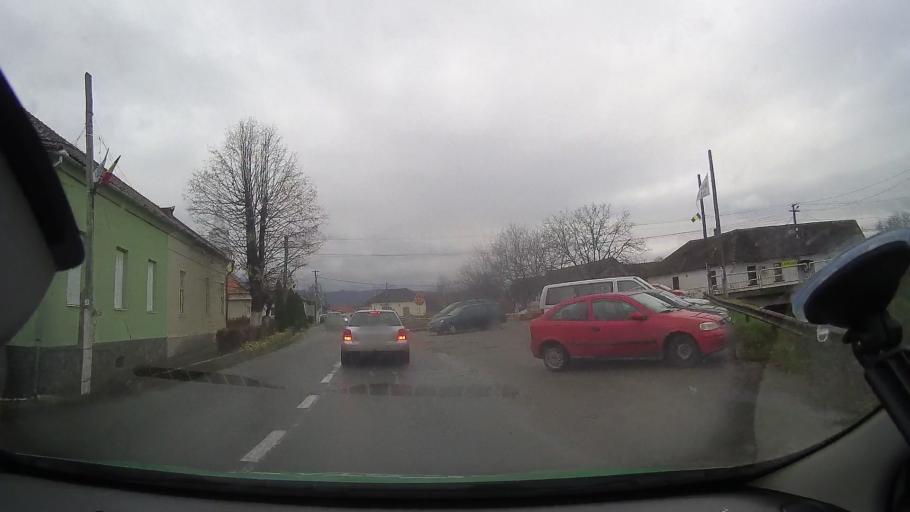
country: RO
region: Arad
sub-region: Comuna Buteni
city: Buteni
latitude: 46.3281
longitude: 22.1232
